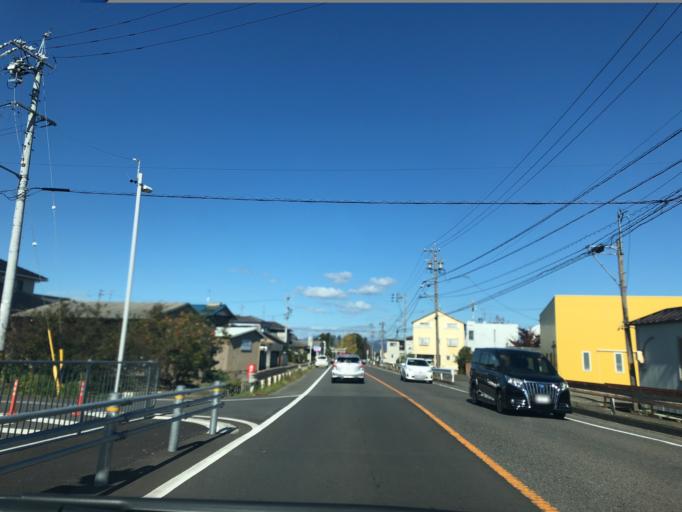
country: JP
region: Gifu
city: Ogaki
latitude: 35.3799
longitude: 136.6684
